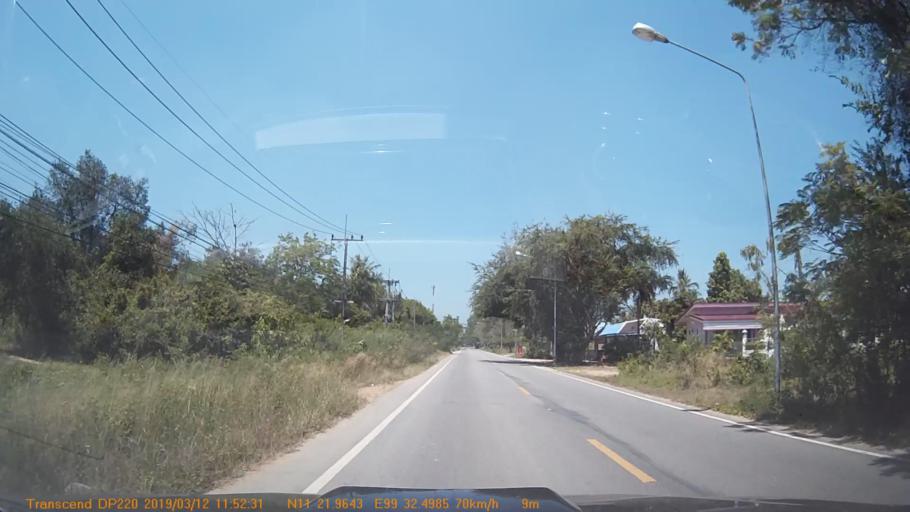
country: TH
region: Prachuap Khiri Khan
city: Thap Sakae
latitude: 11.3661
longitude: 99.5416
